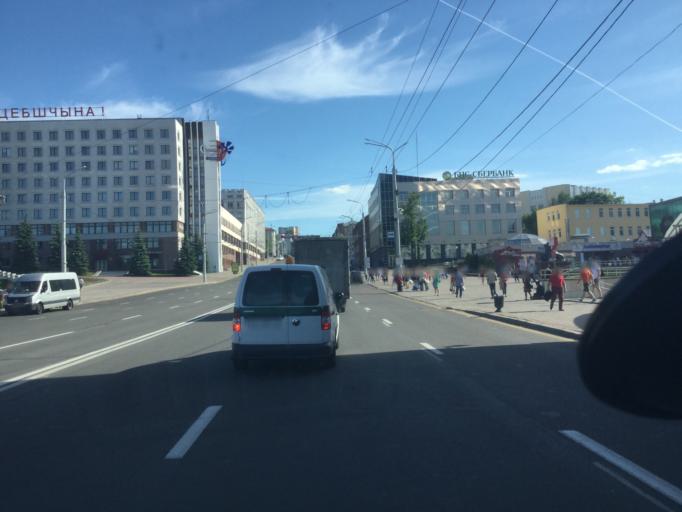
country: BY
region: Vitebsk
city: Vitebsk
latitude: 55.1919
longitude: 30.2061
